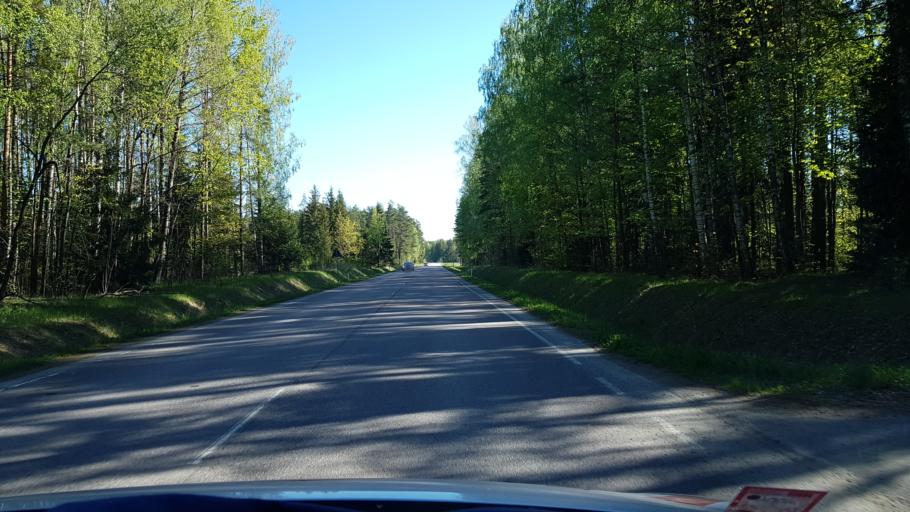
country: EE
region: Polvamaa
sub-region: Polva linn
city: Polva
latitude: 58.0987
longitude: 27.0974
